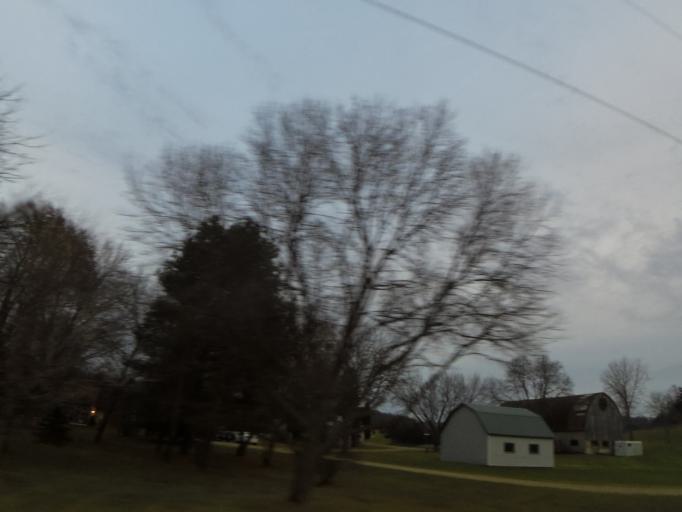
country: US
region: Wisconsin
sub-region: Pierce County
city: River Falls
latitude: 44.8832
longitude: -92.5987
